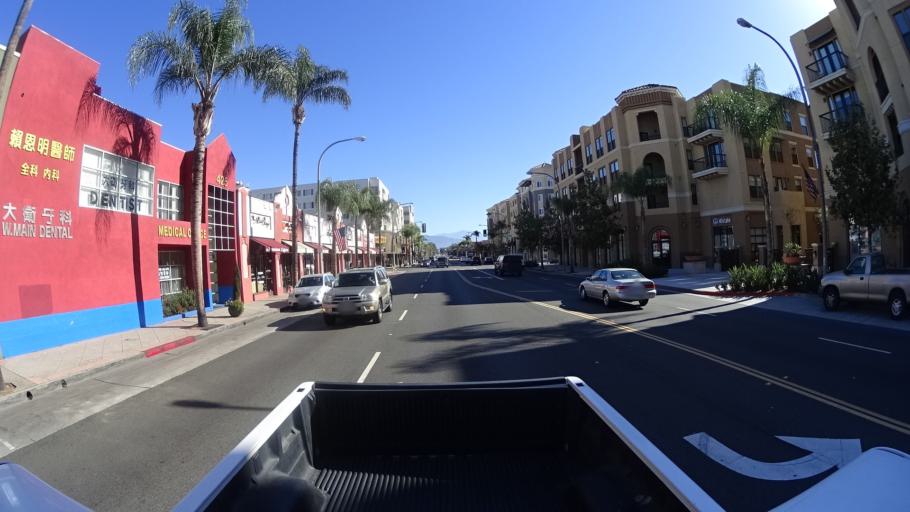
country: US
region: California
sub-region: Los Angeles County
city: Alhambra
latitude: 34.0929
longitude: -118.1317
